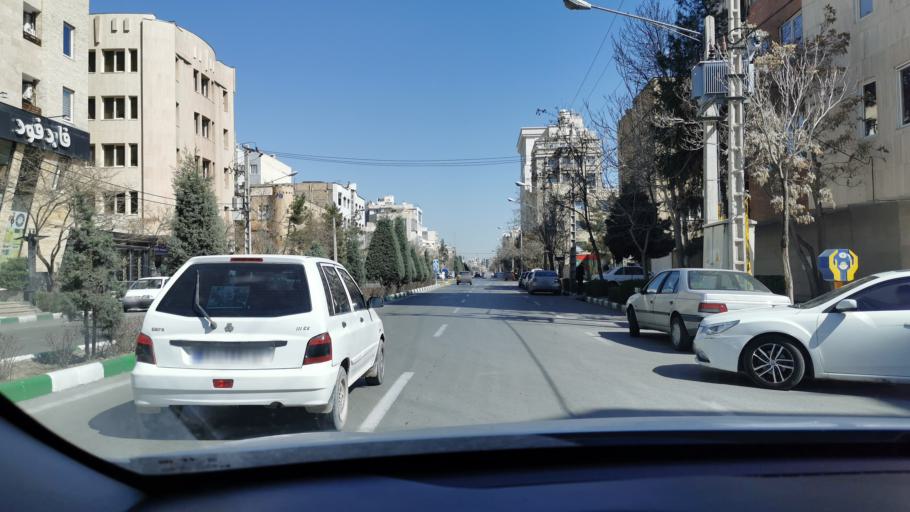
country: IR
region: Razavi Khorasan
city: Mashhad
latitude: 36.3222
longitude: 59.5256
